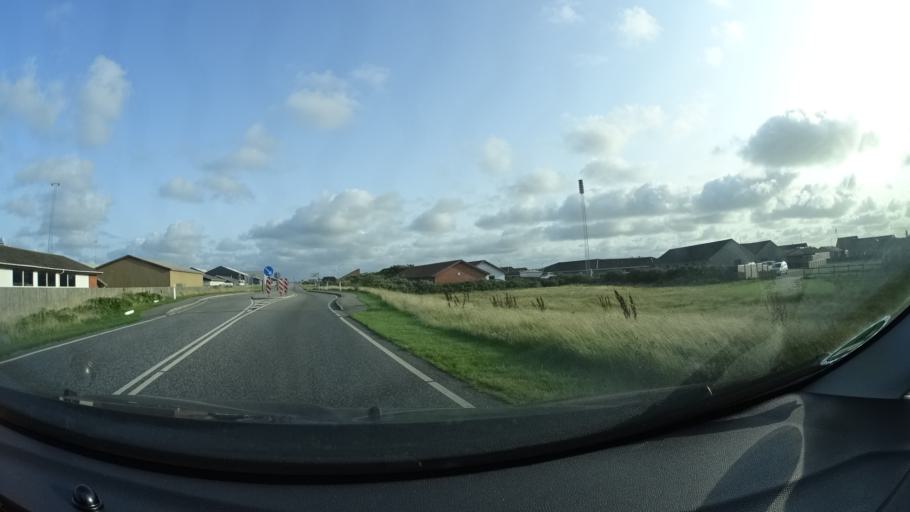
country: DK
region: Central Jutland
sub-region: Lemvig Kommune
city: Thyboron
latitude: 56.7000
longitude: 8.2144
